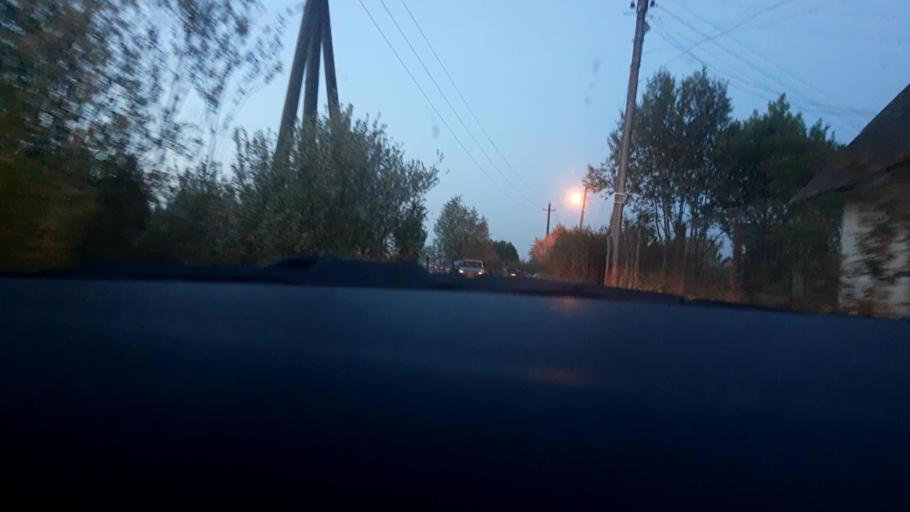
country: RU
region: Bashkortostan
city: Iglino
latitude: 54.7617
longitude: 56.3315
